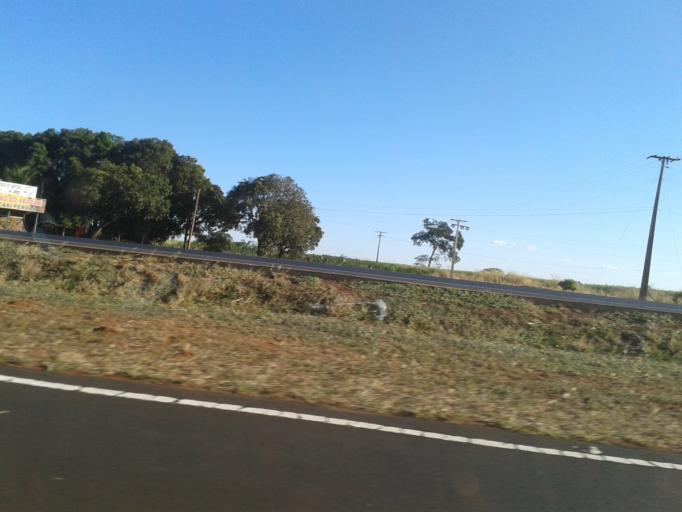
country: BR
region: Minas Gerais
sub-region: Centralina
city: Centralina
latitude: -18.7163
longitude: -49.1294
